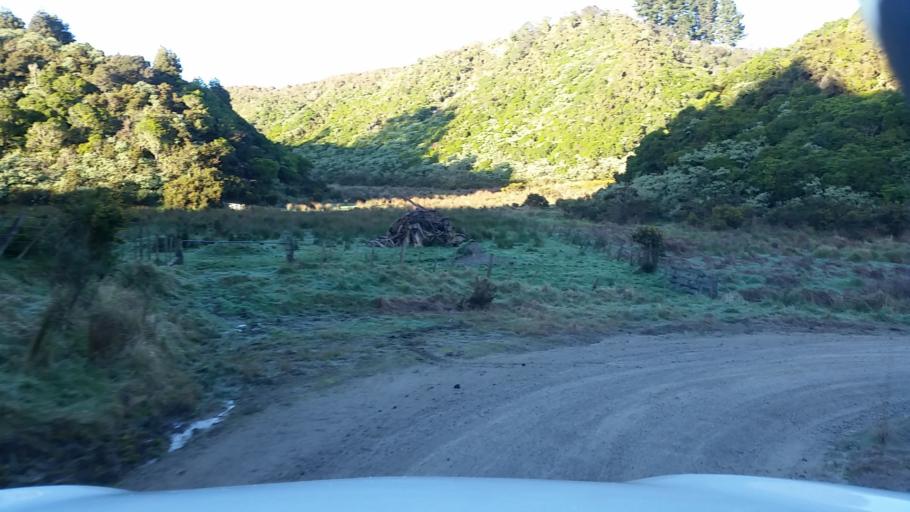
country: NZ
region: Taranaki
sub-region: South Taranaki District
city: Patea
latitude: -39.7605
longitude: 174.7358
